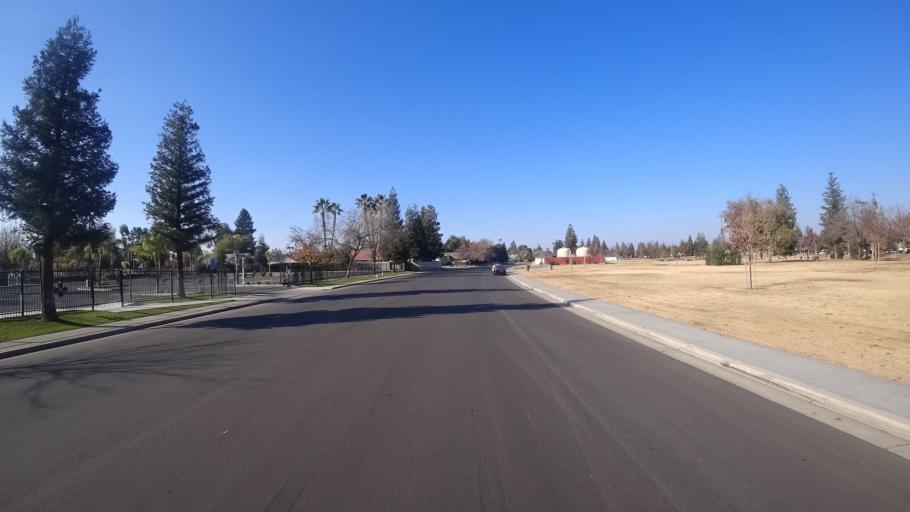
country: US
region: California
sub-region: Kern County
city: Greenacres
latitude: 35.3252
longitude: -119.1040
